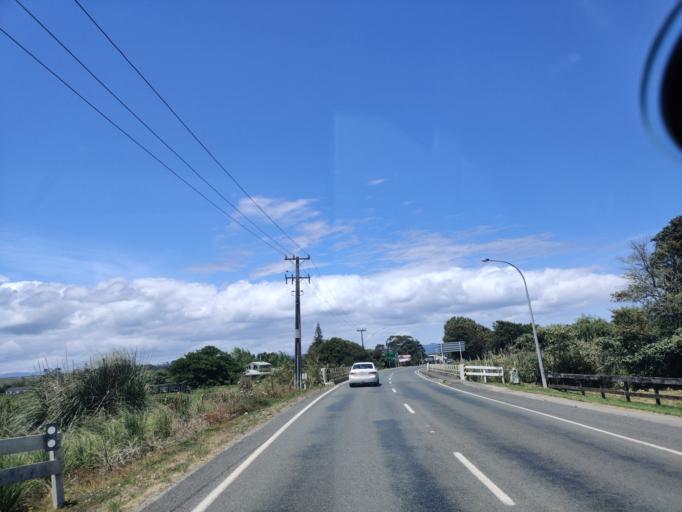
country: NZ
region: Northland
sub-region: Far North District
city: Kaitaia
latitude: -35.0438
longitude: 173.2566
